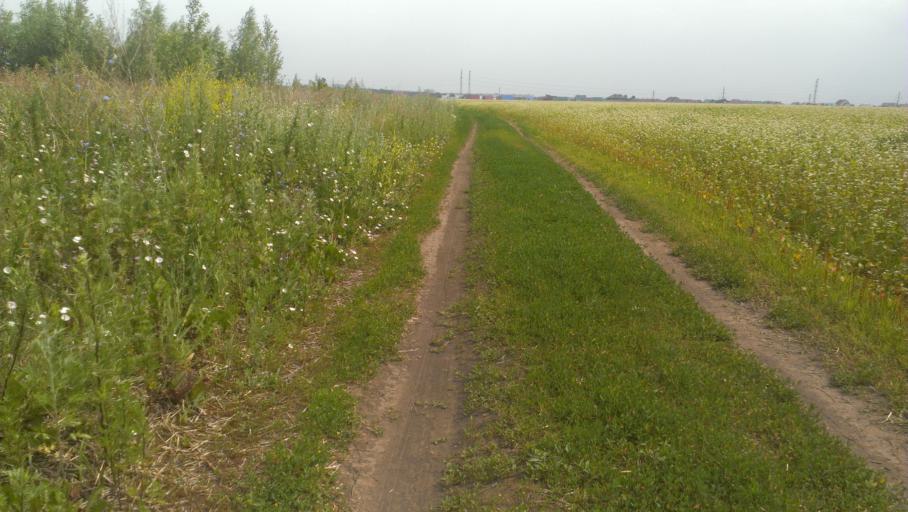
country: RU
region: Altai Krai
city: Novosilikatnyy
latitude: 53.3762
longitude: 83.6418
